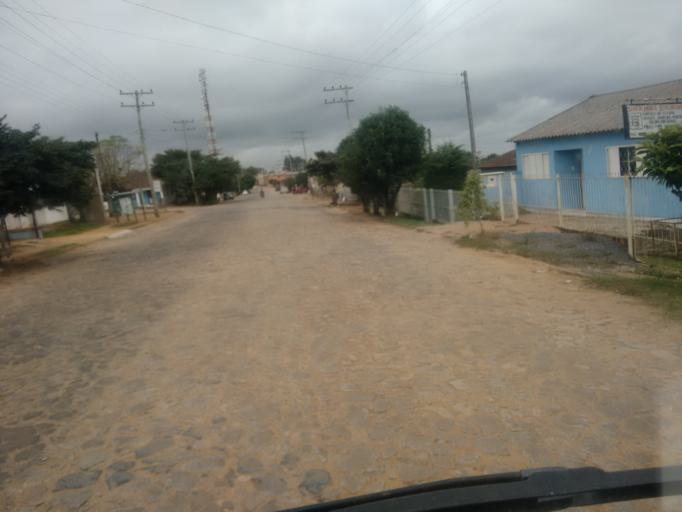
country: BR
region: Rio Grande do Sul
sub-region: Camaqua
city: Camaqua
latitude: -30.8369
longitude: -51.8212
